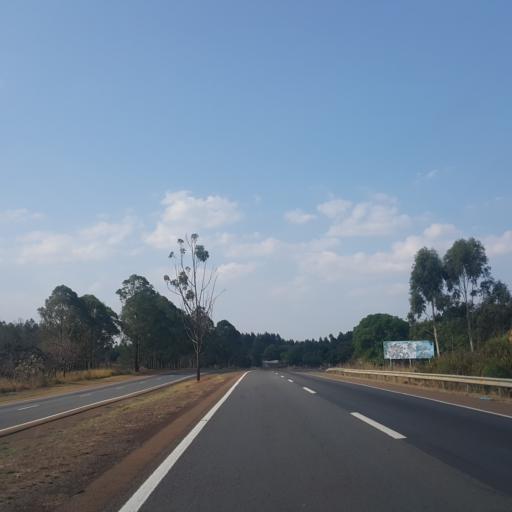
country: BR
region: Goias
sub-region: Abadiania
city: Abadiania
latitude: -16.1865
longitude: -48.6984
